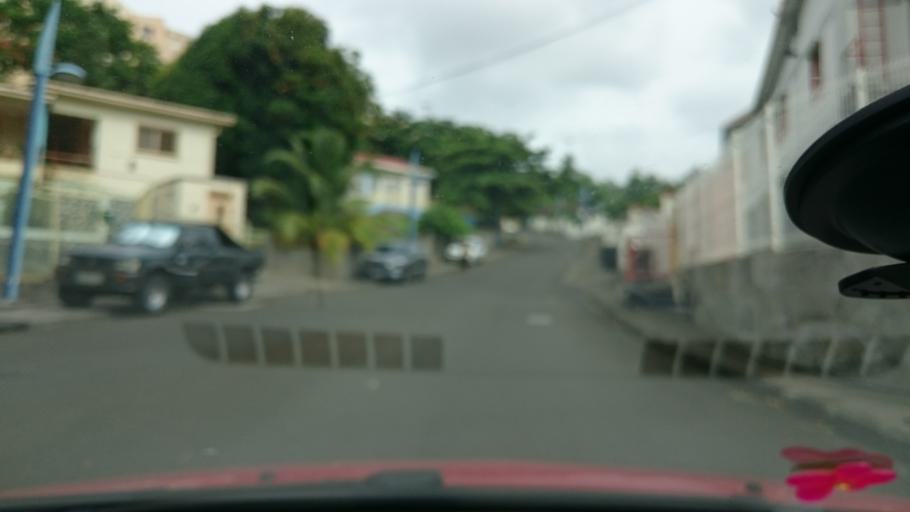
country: MQ
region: Martinique
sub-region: Martinique
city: Riviere-Pilote
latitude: 14.4826
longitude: -60.9057
